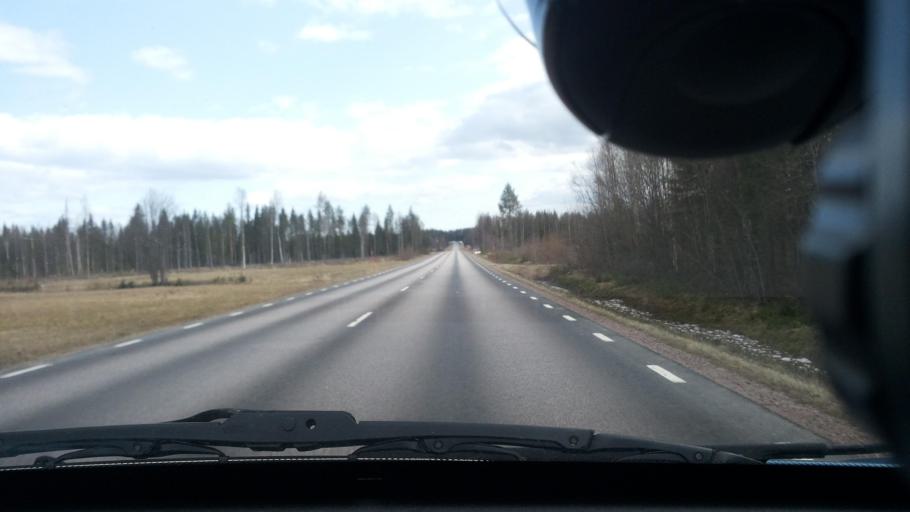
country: SE
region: Norrbotten
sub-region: Lulea Kommun
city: Sodra Sunderbyn
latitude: 65.6168
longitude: 21.9472
